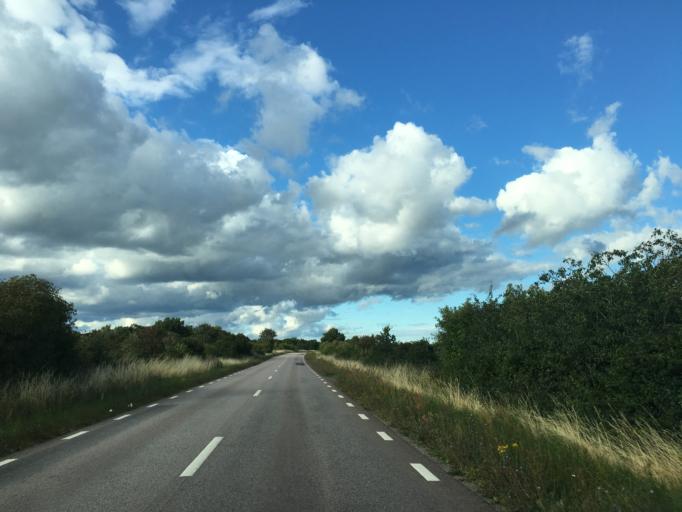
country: SE
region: Kalmar
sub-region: Morbylanga Kommun
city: Moerbylanga
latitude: 56.5513
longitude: 16.4432
